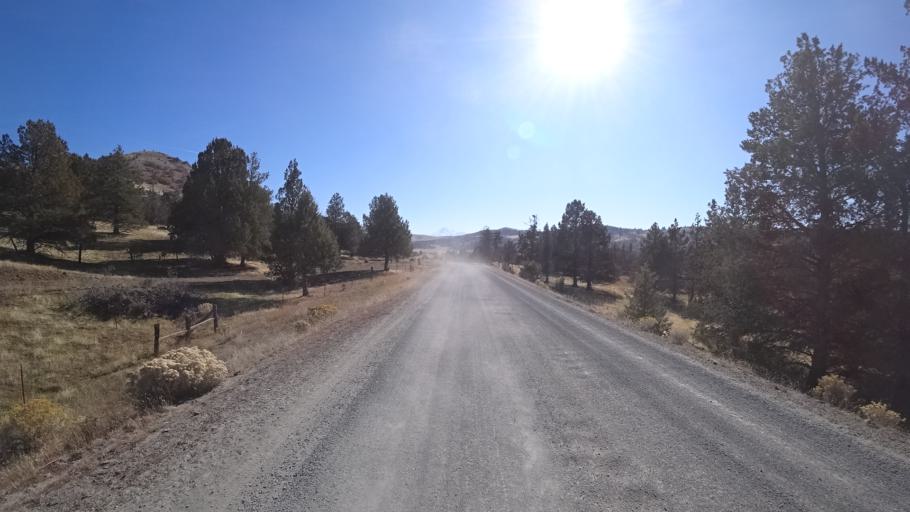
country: US
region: California
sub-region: Siskiyou County
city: Montague
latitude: 41.8039
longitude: -122.3706
